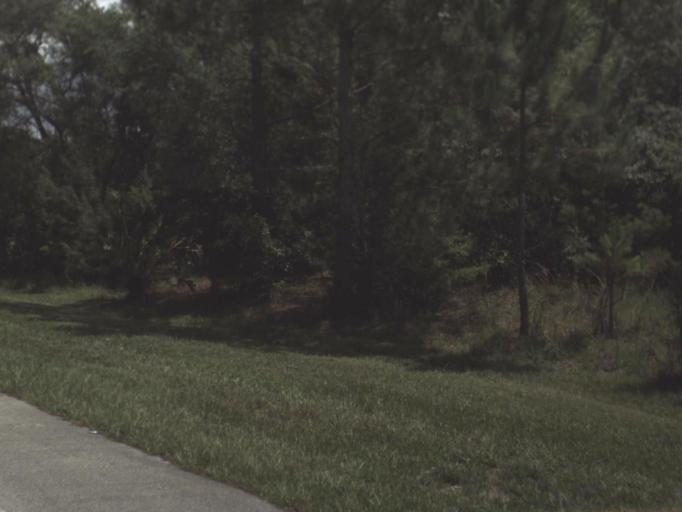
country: US
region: Florida
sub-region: Putnam County
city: Crescent City
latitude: 29.3831
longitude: -81.5087
